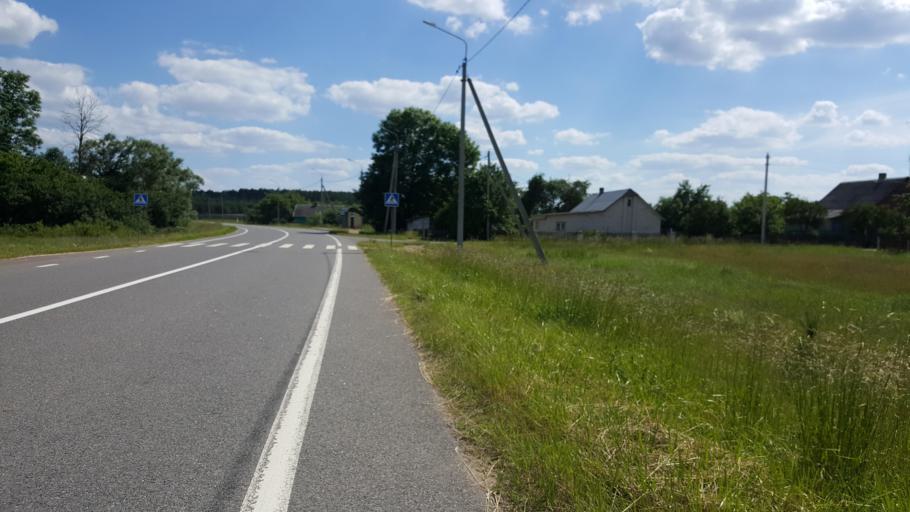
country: BY
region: Brest
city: Kamyanyuki
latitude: 52.5261
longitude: 23.6558
